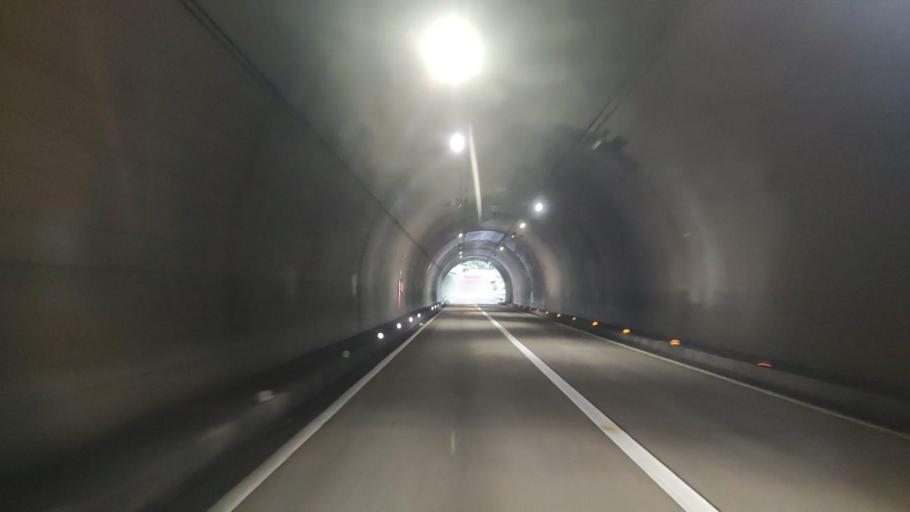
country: JP
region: Wakayama
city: Shingu
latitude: 33.8074
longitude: 135.7104
